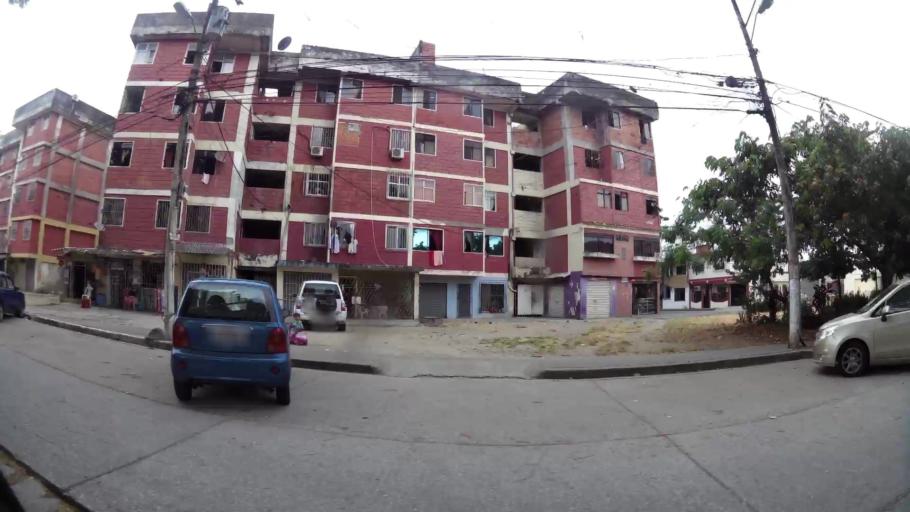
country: EC
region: Guayas
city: Eloy Alfaro
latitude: -2.1242
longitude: -79.8867
